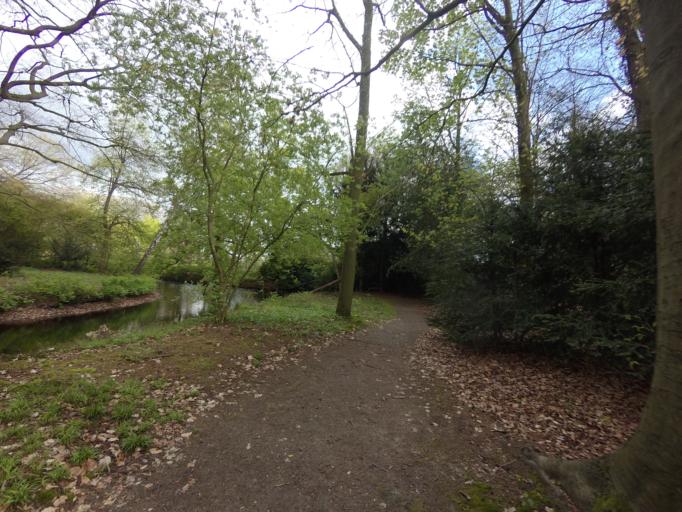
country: NL
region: Utrecht
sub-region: Gemeente De Bilt
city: De Bilt
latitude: 52.1006
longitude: 5.1721
